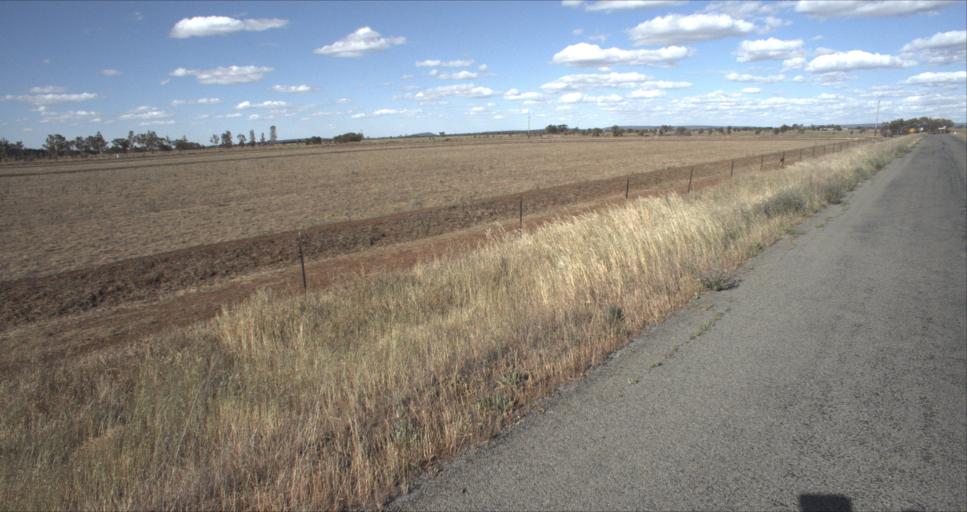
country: AU
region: New South Wales
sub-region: Leeton
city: Leeton
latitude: -34.4438
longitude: 146.2528
